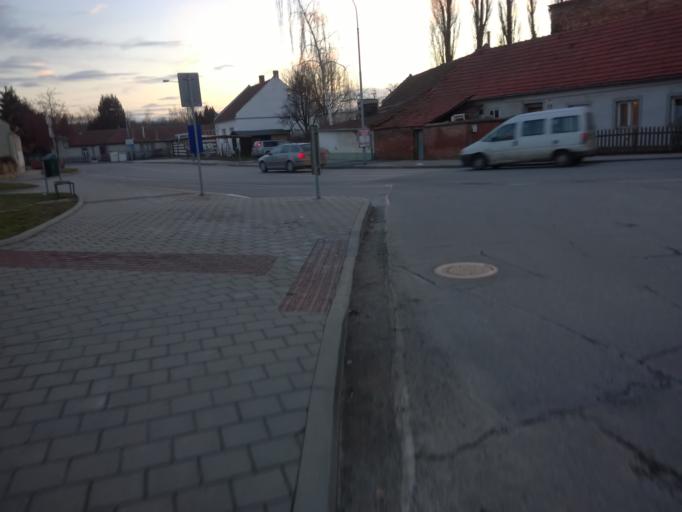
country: CZ
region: South Moravian
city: Ostopovice
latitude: 49.1664
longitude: 16.5587
